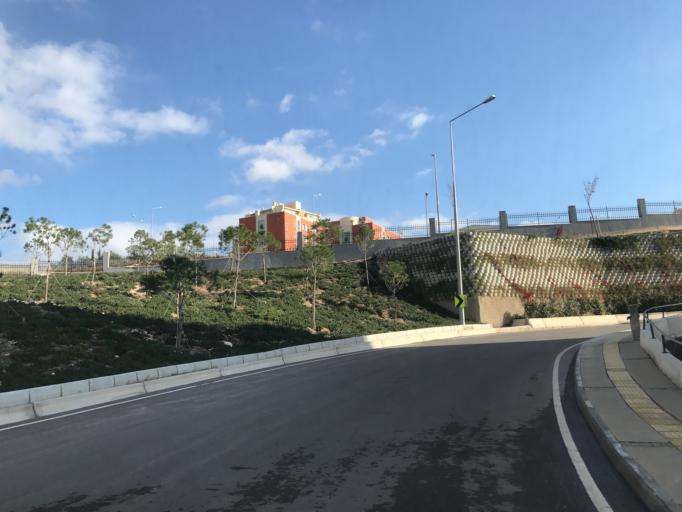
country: TR
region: Izmir
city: Buca
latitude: 38.4006
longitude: 27.2016
